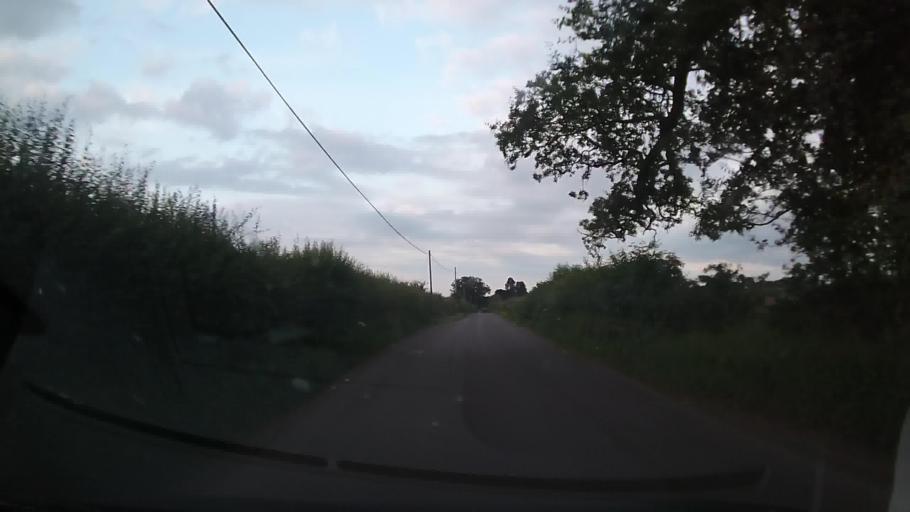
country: GB
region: England
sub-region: Shropshire
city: Petton
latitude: 52.8100
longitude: -2.7775
